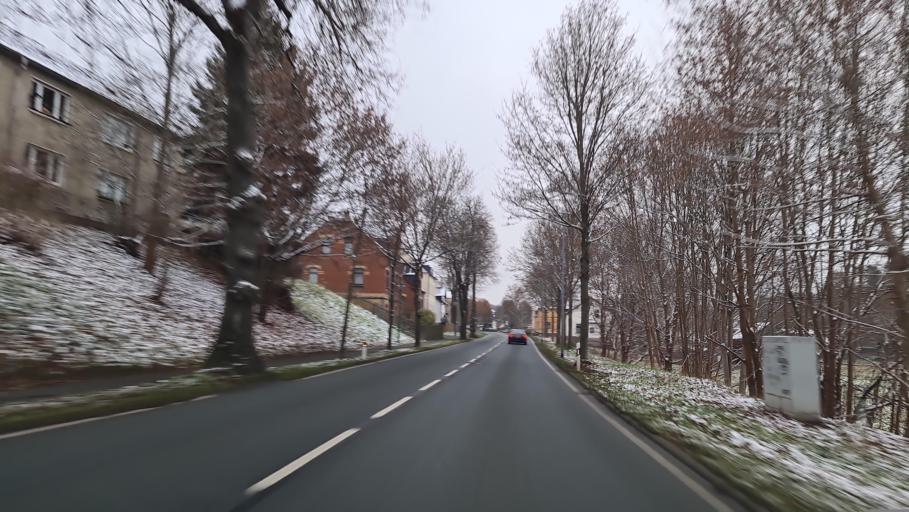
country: DE
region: Saxony
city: Adorf
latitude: 50.3176
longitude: 12.2733
